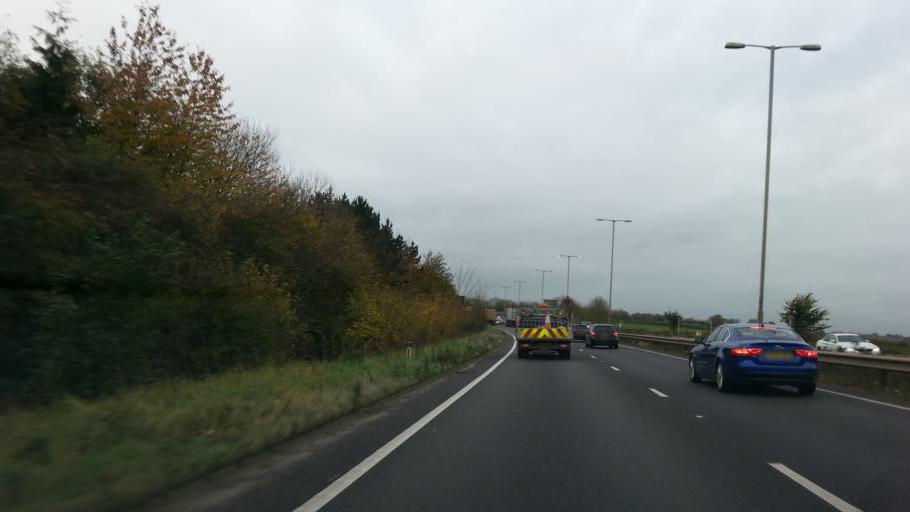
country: GB
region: England
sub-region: Northamptonshire
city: Rothwell
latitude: 52.4133
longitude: -0.7754
